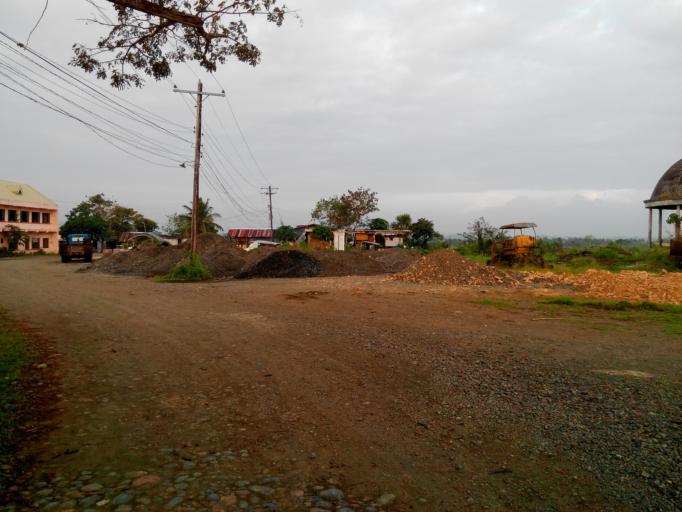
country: PH
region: Western Visayas
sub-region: Province of Iloilo
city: Passi
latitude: 11.1178
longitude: 122.6469
